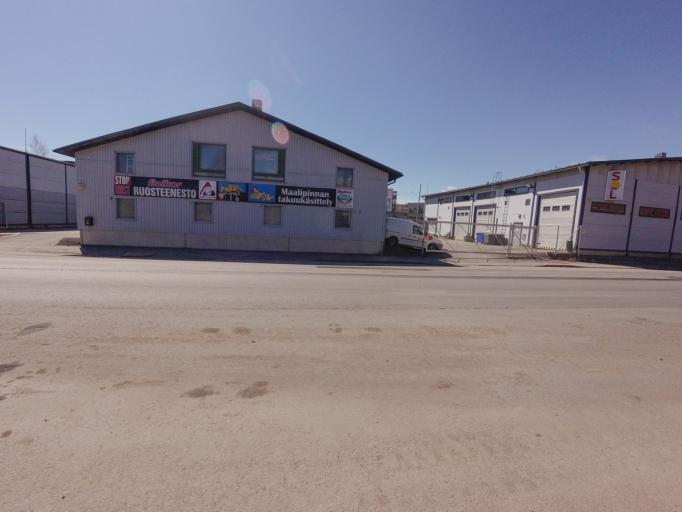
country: FI
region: Uusimaa
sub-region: Helsinki
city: Helsinki
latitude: 60.1974
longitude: 24.9731
